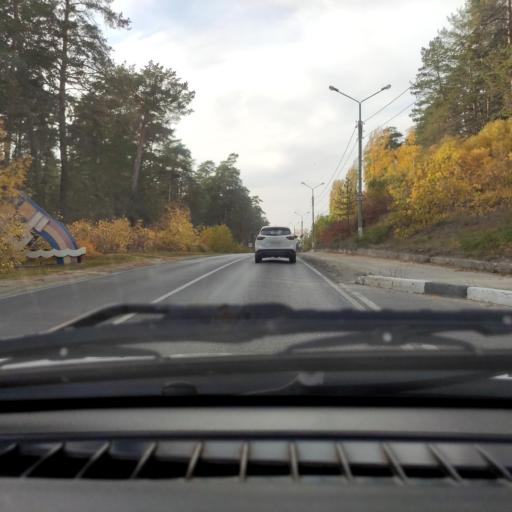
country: RU
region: Samara
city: Tol'yatti
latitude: 53.4756
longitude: 49.3438
